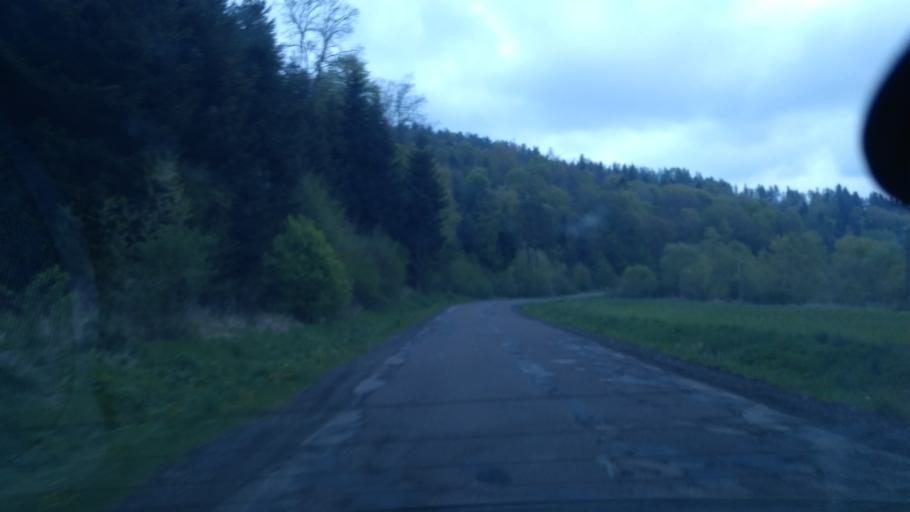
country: PL
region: Subcarpathian Voivodeship
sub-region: Powiat brzozowski
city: Nozdrzec
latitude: 49.7360
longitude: 22.2034
